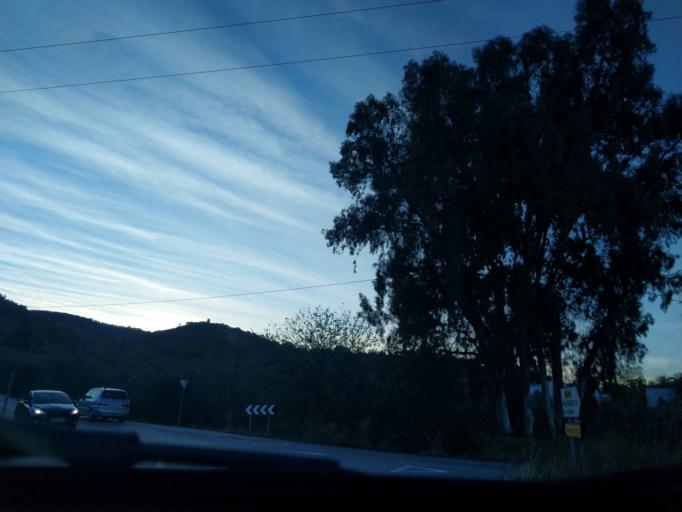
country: ES
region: Extremadura
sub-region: Provincia de Badajoz
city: Reina
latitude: 38.1625
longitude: -5.8984
